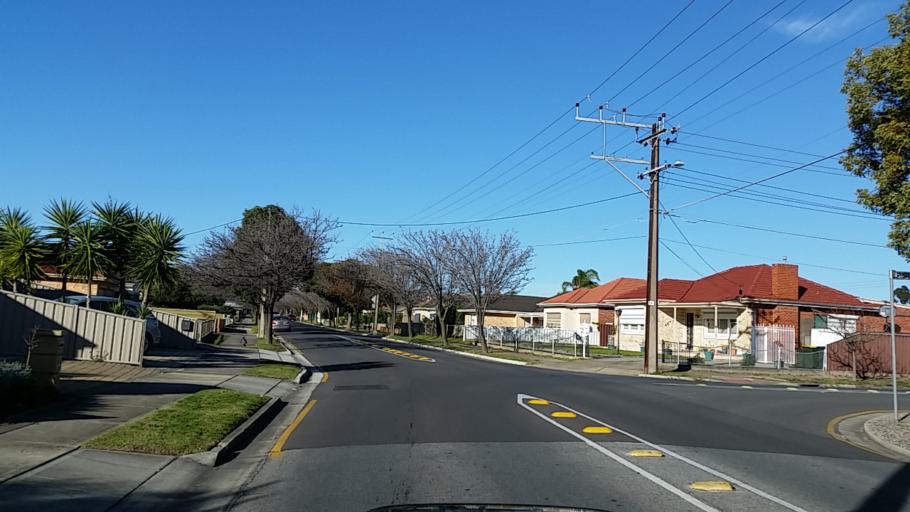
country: AU
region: South Australia
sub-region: City of West Torrens
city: Plympton
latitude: -34.9568
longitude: 138.5495
